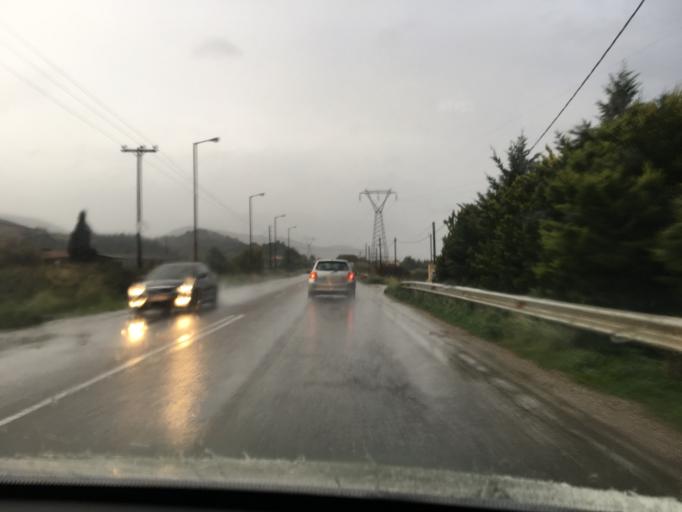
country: GR
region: West Greece
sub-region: Nomos Aitolias kai Akarnanias
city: Antirrio
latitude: 38.3464
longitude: 21.7707
